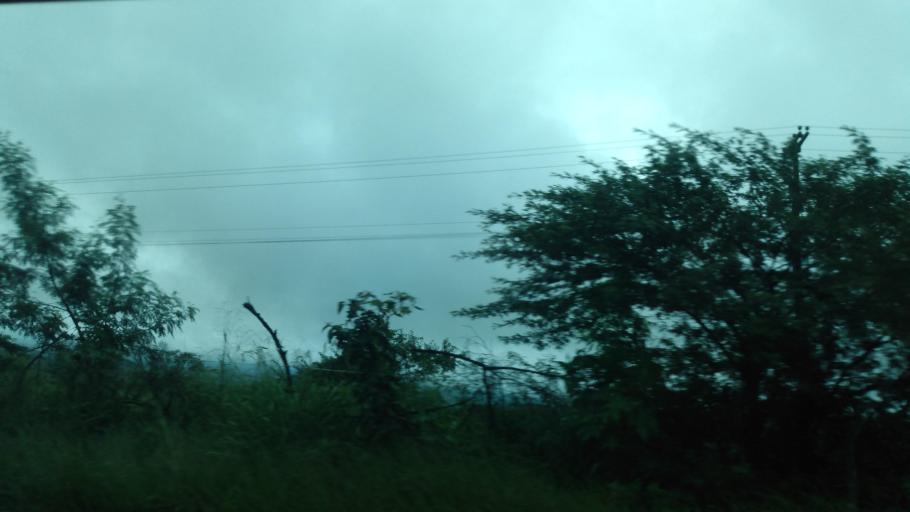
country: BR
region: Pernambuco
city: Garanhuns
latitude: -8.8745
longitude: -36.5222
